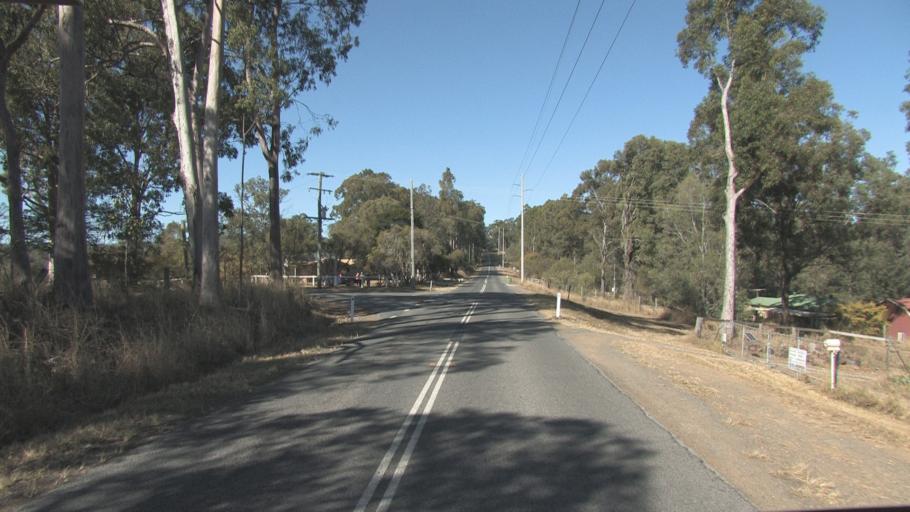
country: AU
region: Queensland
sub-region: Logan
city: Cedar Vale
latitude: -27.8820
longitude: 153.0159
